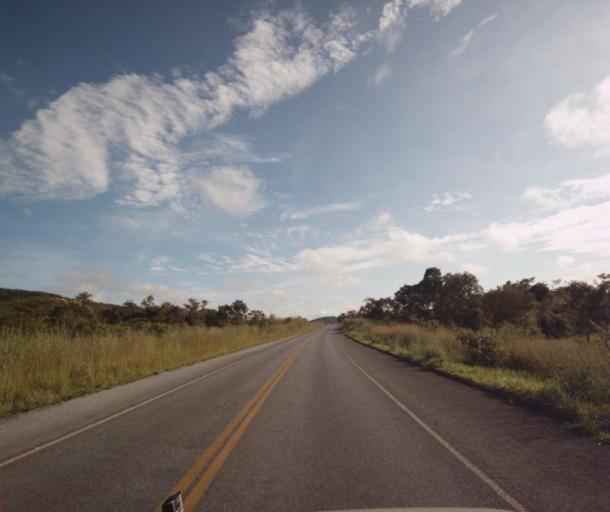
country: BR
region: Goias
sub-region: Pirenopolis
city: Pirenopolis
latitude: -15.5558
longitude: -48.6230
